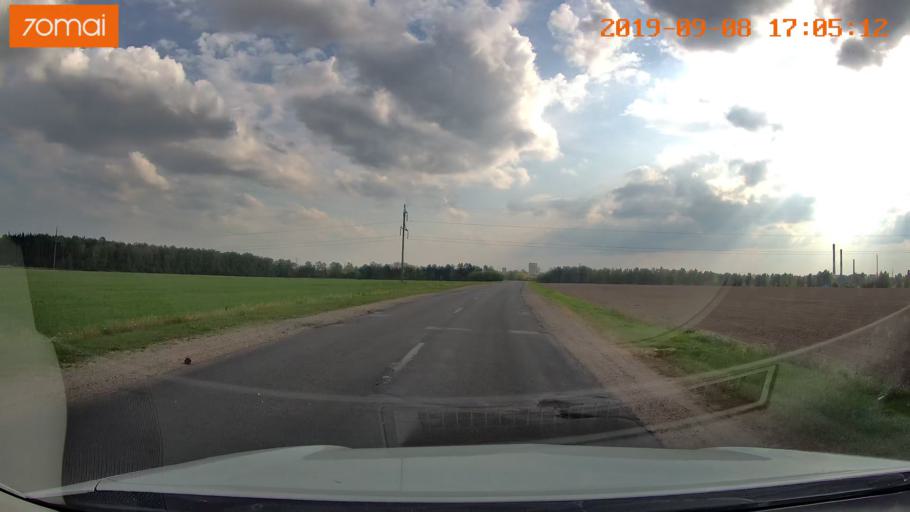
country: BY
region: Grodnenskaya
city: Hrodna
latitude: 53.6808
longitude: 23.9558
